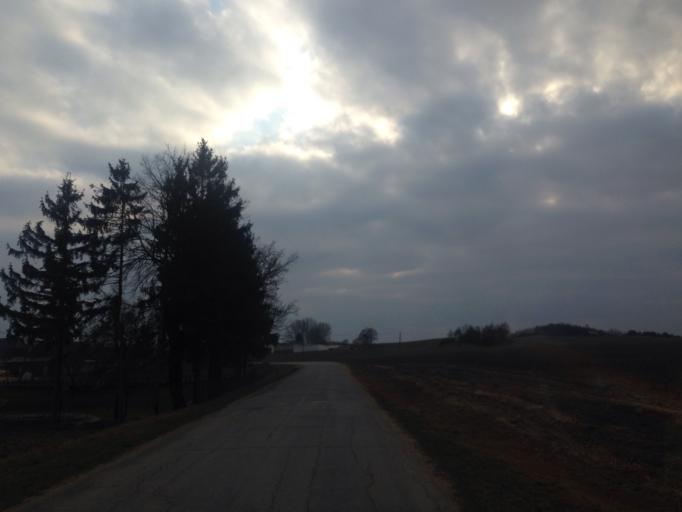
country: PL
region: Warmian-Masurian Voivodeship
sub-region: Powiat dzialdowski
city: Lidzbark
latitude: 53.3558
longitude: 19.7628
